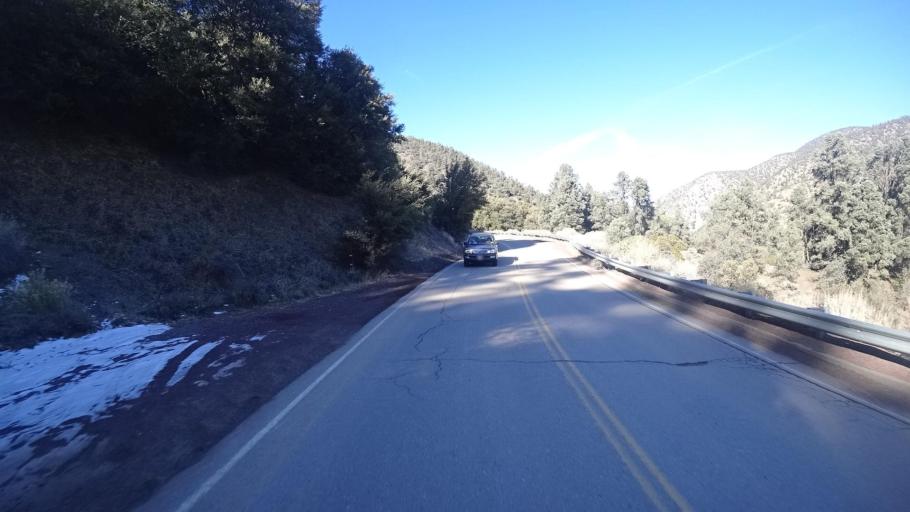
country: US
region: California
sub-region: Kern County
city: Pine Mountain Club
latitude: 34.8524
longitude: -119.1248
